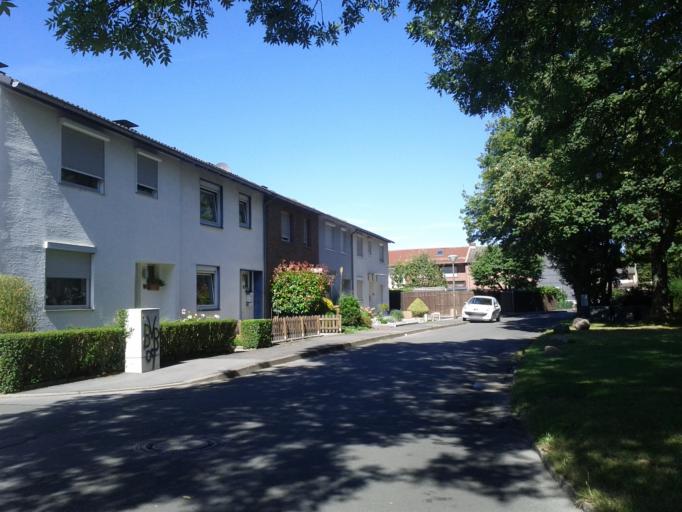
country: DE
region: North Rhine-Westphalia
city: Lanstrop
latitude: 51.5507
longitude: 7.5285
